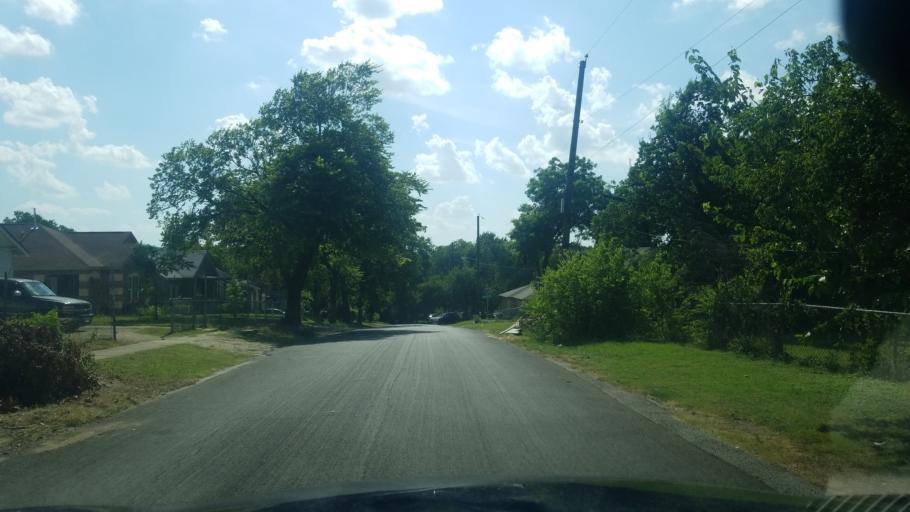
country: US
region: Texas
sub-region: Dallas County
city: Dallas
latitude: 32.7271
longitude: -96.8069
